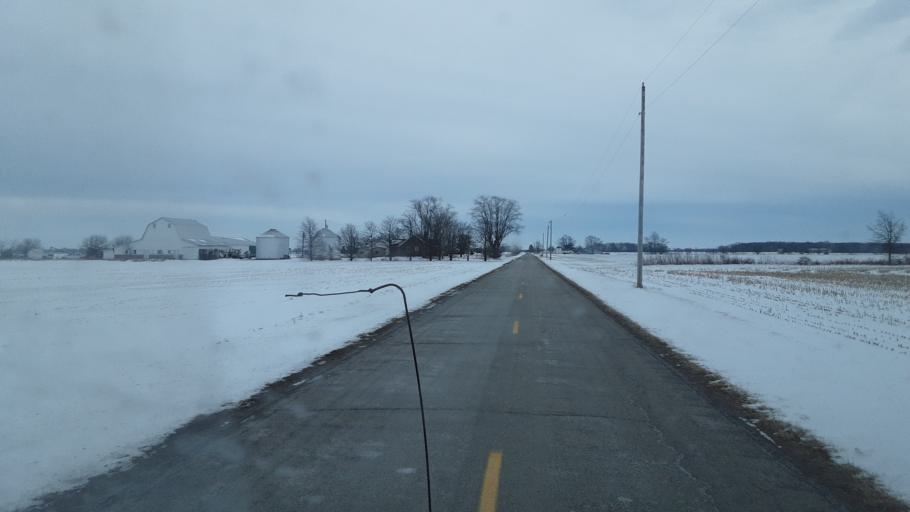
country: US
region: Ohio
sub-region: Madison County
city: Bethel
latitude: 39.7123
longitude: -83.3515
